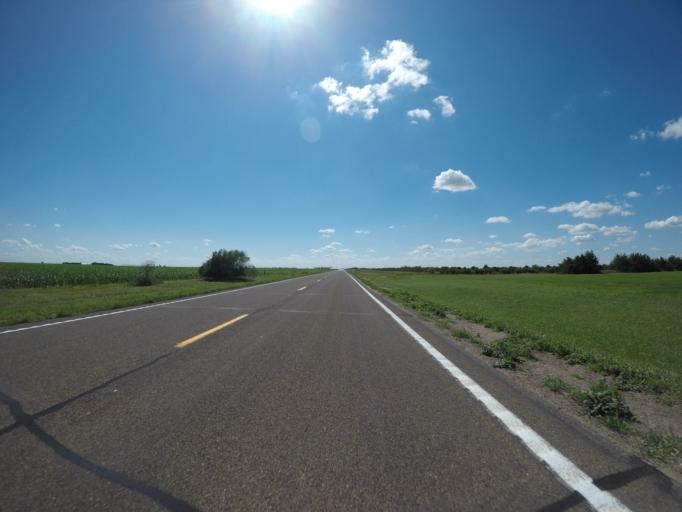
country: US
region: Nebraska
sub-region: Chase County
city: Imperial
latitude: 40.5377
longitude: -101.8837
